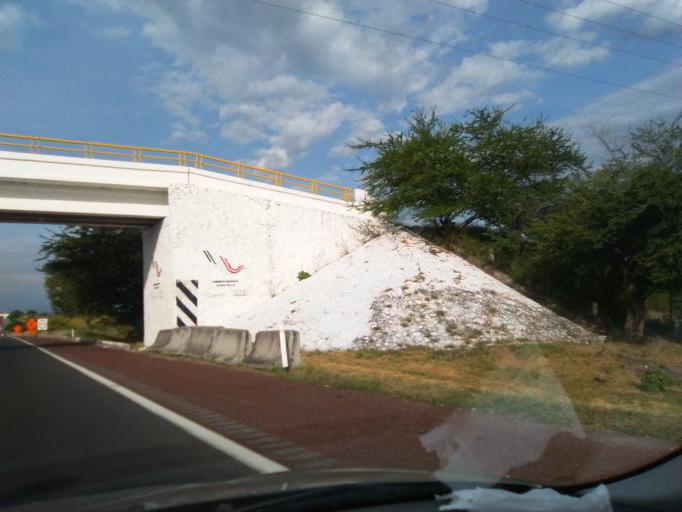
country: MX
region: Morelos
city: Xoxocotla
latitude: 18.7031
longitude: -99.2751
